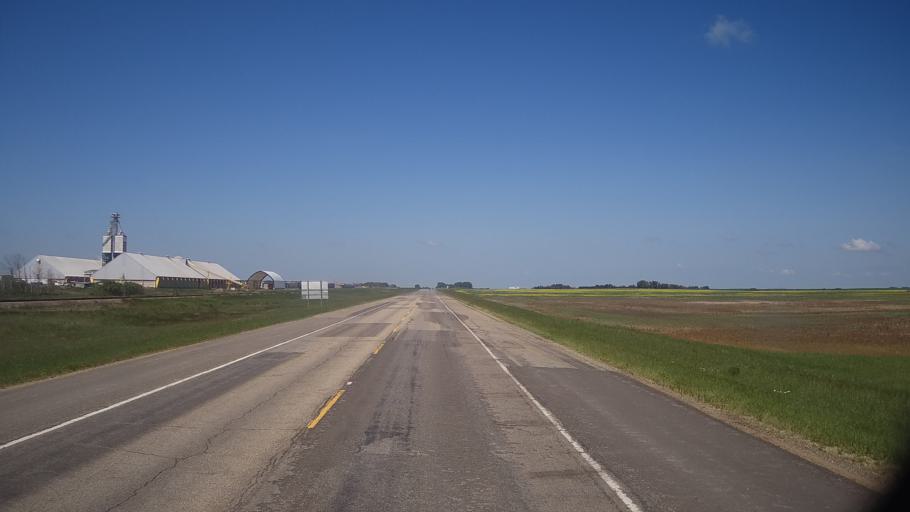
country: CA
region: Saskatchewan
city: Saskatoon
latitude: 51.9926
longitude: -106.0840
